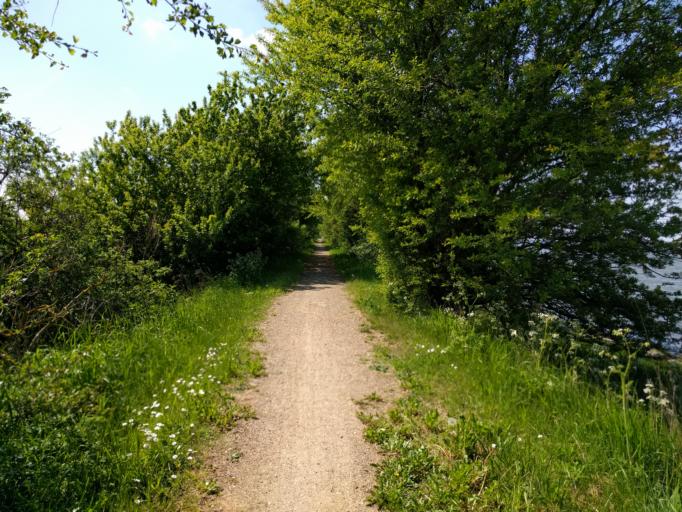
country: DK
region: Zealand
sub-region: Guldborgsund Kommune
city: Stubbekobing
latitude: 54.8879
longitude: 12.1015
